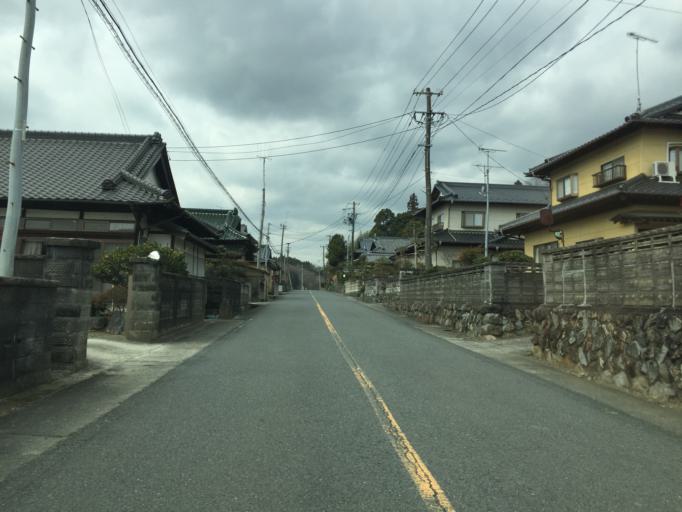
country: JP
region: Fukushima
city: Iwaki
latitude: 36.9984
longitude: 140.8036
